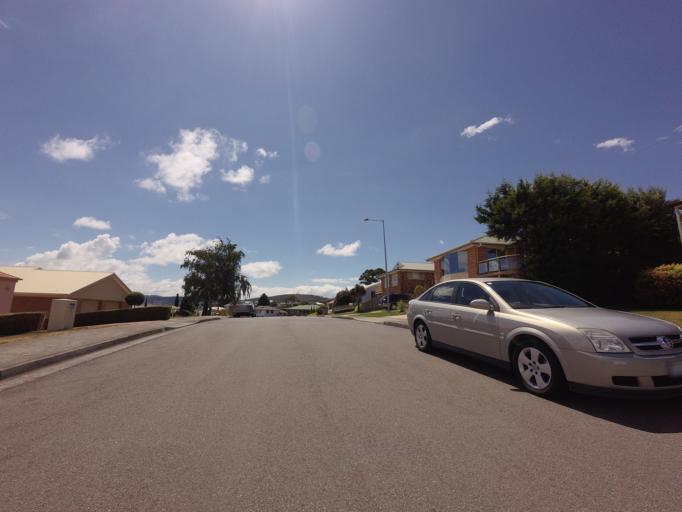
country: AU
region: Tasmania
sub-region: Clarence
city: Howrah
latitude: -42.9201
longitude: 147.4126
